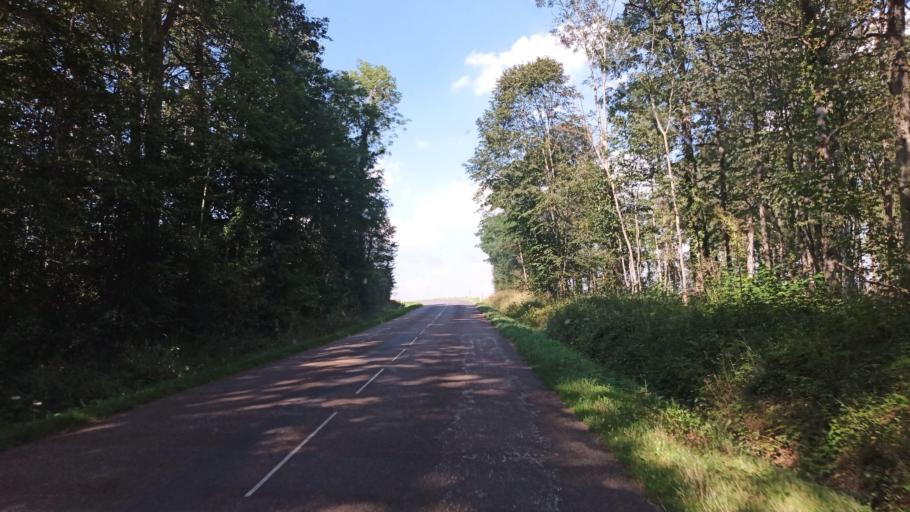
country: FR
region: Bourgogne
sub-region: Departement de l'Yonne
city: Saint-Valerien
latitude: 48.1597
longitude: 3.0989
